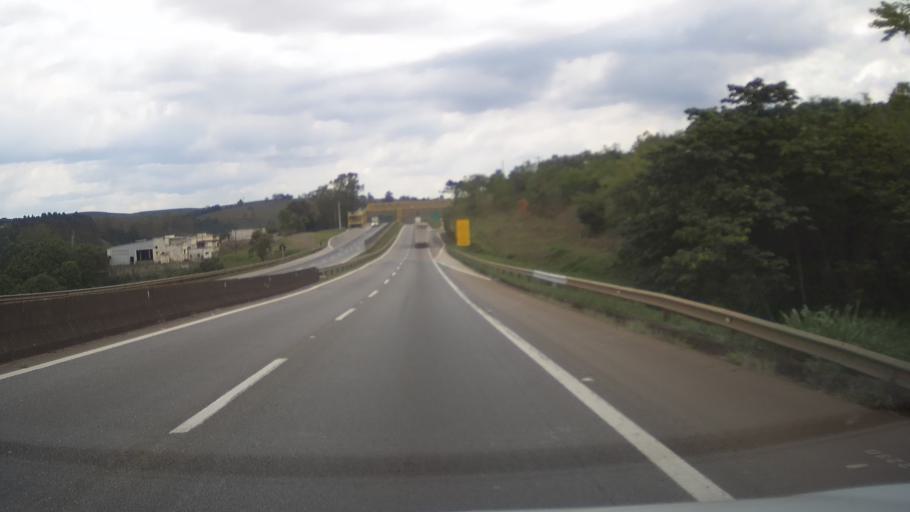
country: BR
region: Minas Gerais
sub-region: Nepomuceno
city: Nepomuceno
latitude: -21.4568
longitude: -45.2109
